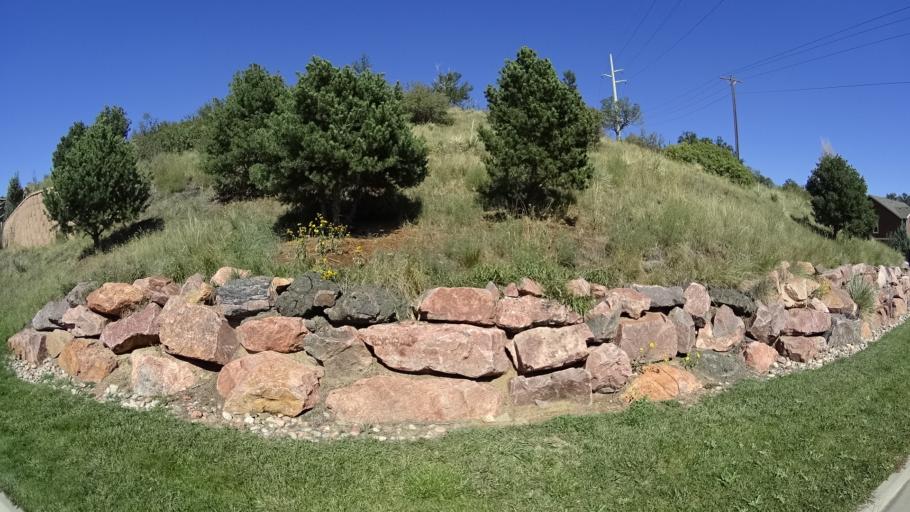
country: US
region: Colorado
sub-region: El Paso County
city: Colorado Springs
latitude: 38.8602
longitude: -104.8515
